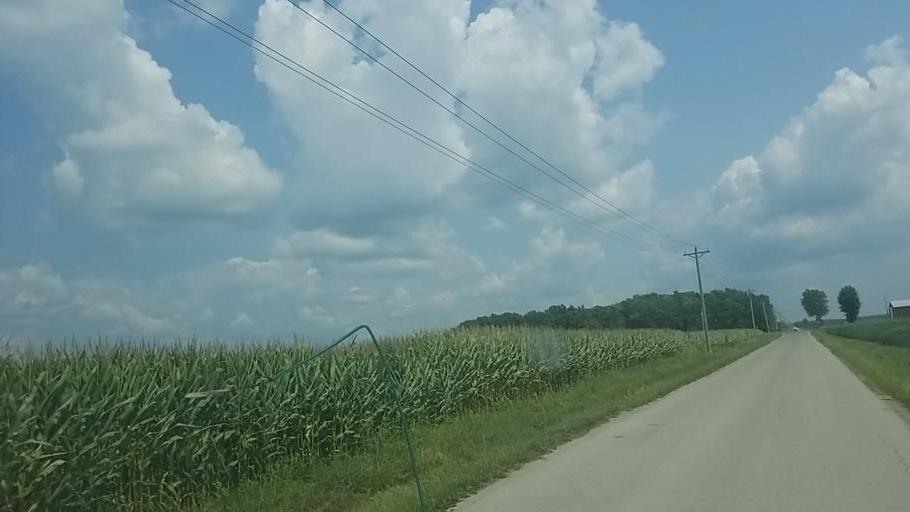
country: US
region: Ohio
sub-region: Wyandot County
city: Upper Sandusky
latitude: 40.9208
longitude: -83.1723
